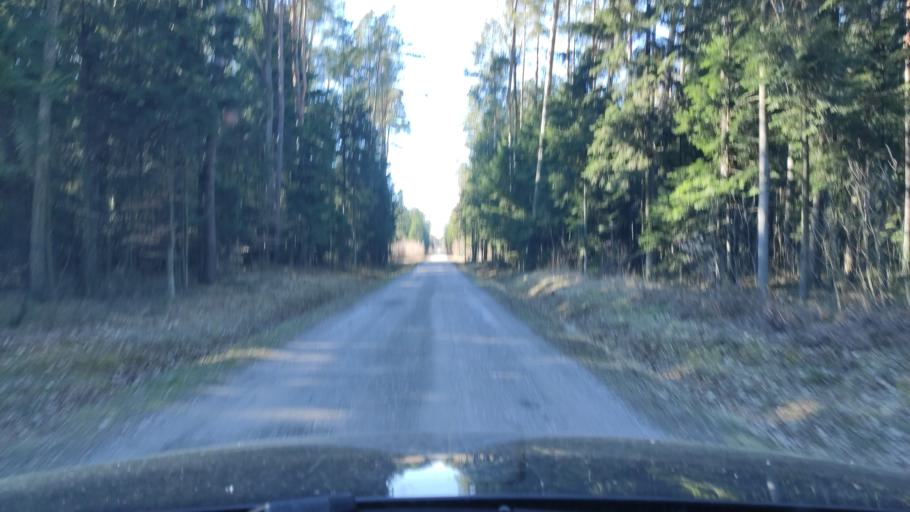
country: PL
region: Masovian Voivodeship
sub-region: Powiat radomski
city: Jedlnia-Letnisko
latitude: 51.4671
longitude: 21.3127
